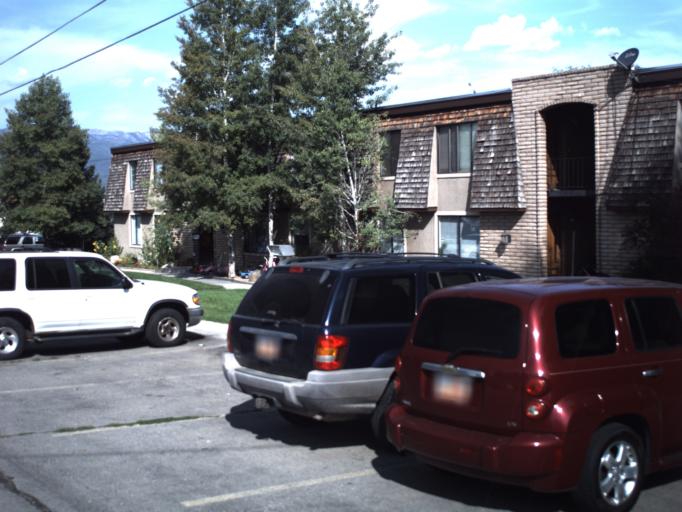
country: US
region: Utah
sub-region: Wasatch County
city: Heber
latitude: 40.5063
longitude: -111.4109
